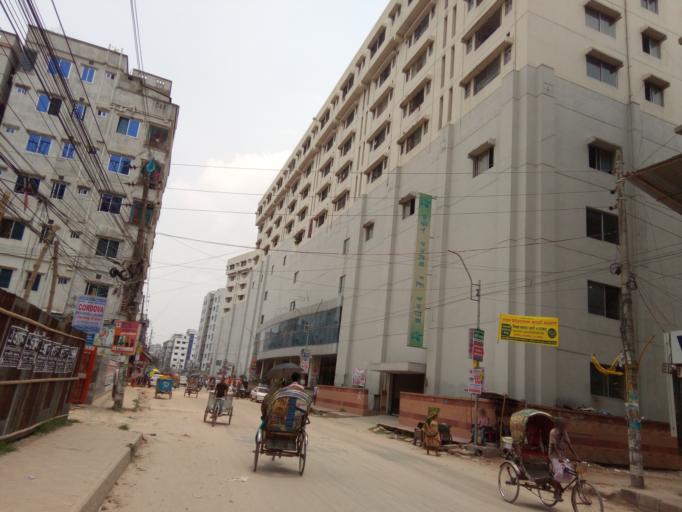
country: BD
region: Dhaka
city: Paltan
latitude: 23.7584
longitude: 90.4416
